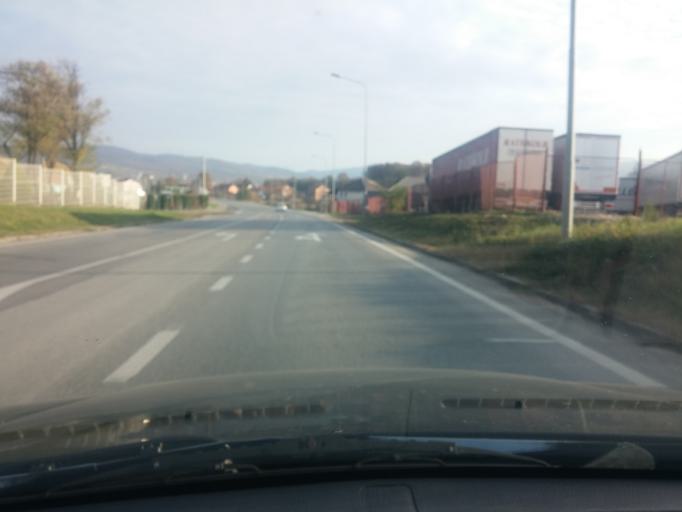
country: BA
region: Republika Srpska
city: Banja Luka
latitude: 44.8236
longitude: 17.1934
